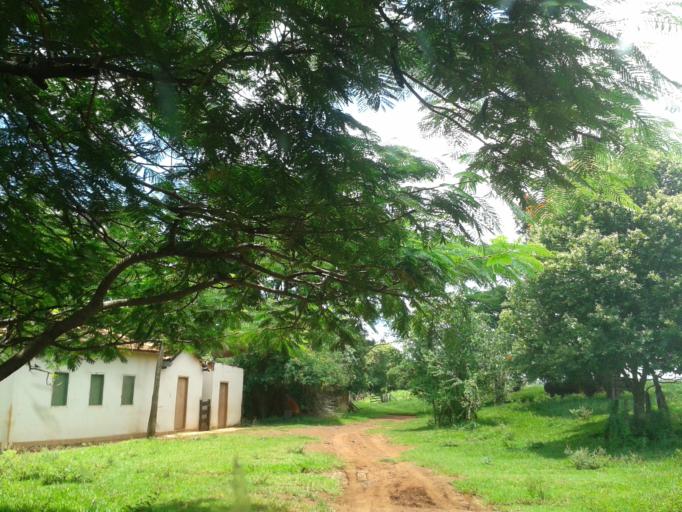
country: BR
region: Minas Gerais
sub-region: Capinopolis
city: Capinopolis
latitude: -18.7846
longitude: -49.8006
